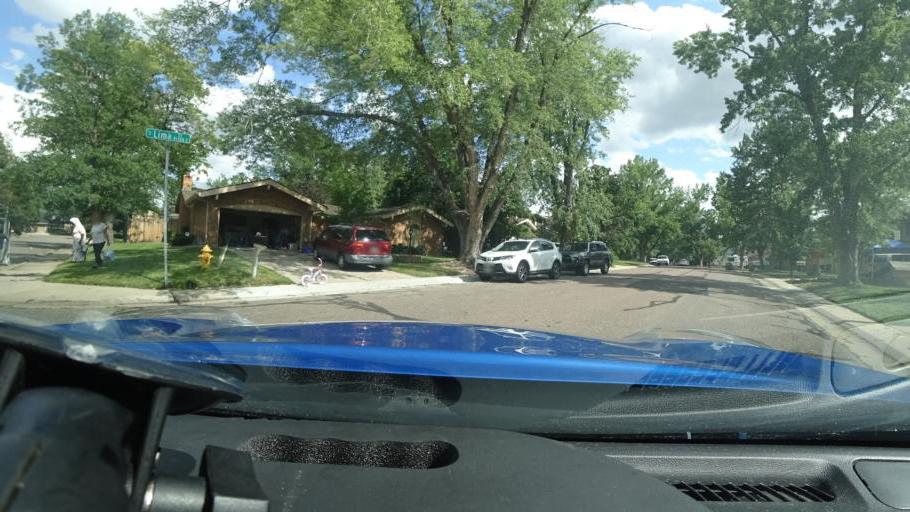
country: US
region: Colorado
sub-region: Adams County
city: Aurora
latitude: 39.6925
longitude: -104.8579
